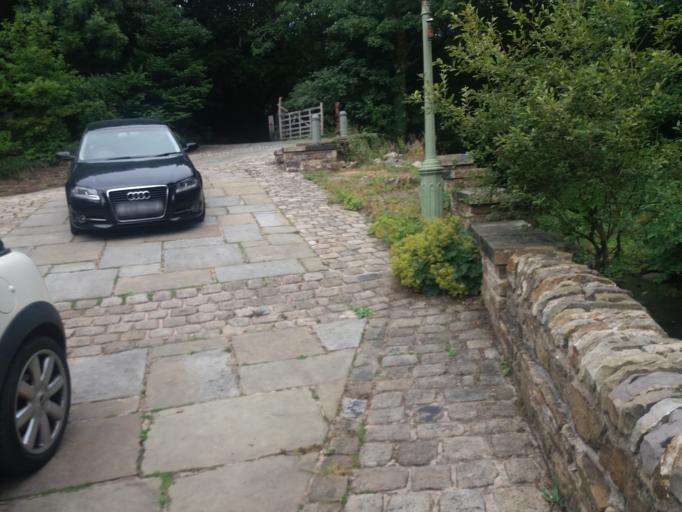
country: GB
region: England
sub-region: Lancashire
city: Chorley
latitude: 53.6418
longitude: -2.6019
